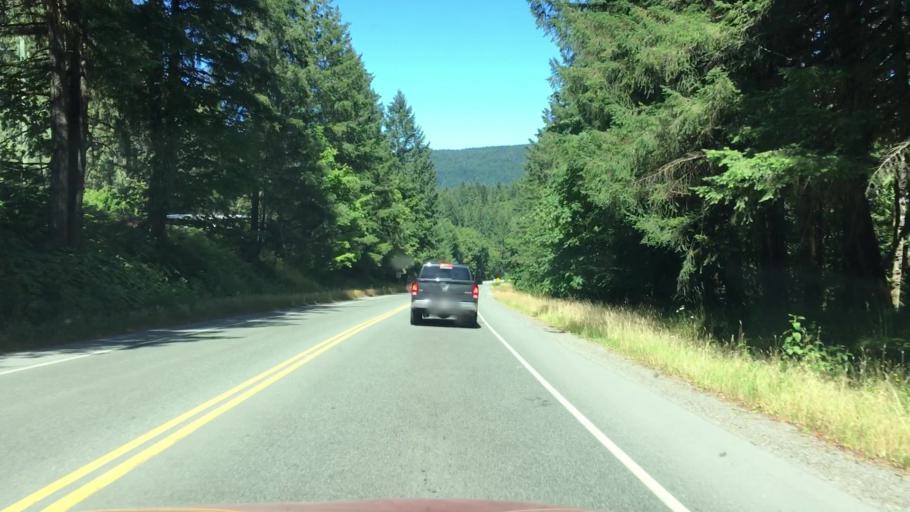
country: CA
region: British Columbia
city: Port Alberni
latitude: 49.2570
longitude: -124.7765
